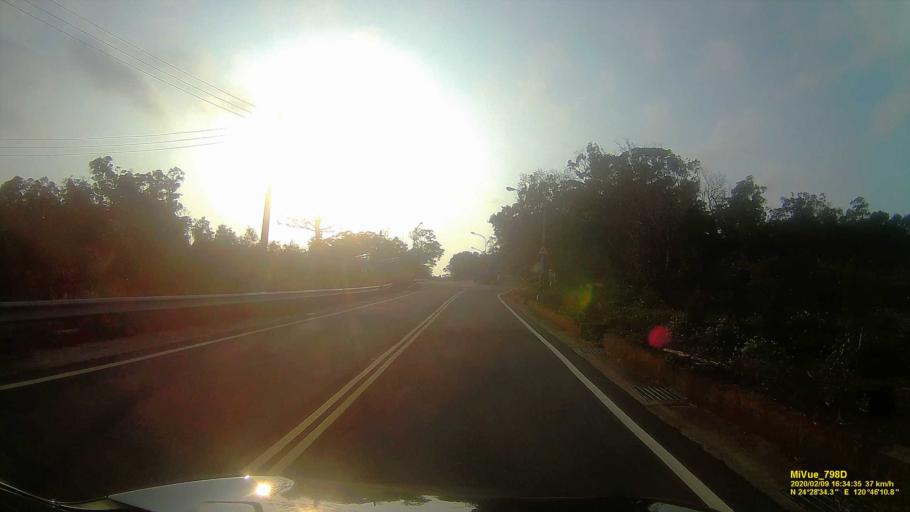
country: TW
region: Taiwan
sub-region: Miaoli
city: Miaoli
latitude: 24.4762
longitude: 120.7695
